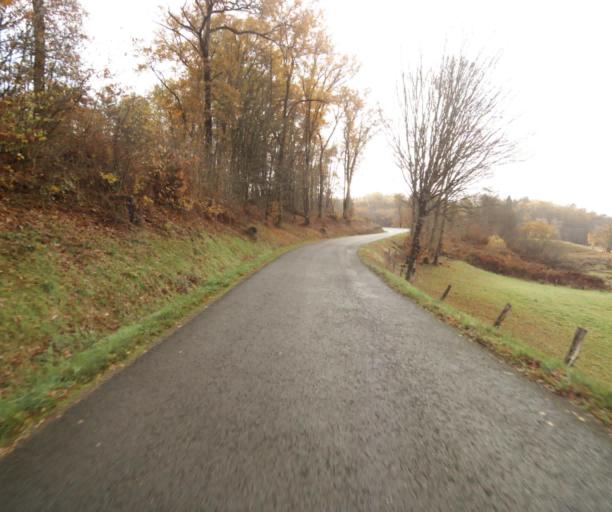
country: FR
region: Limousin
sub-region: Departement de la Correze
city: Saint-Mexant
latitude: 45.2328
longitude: 1.6436
